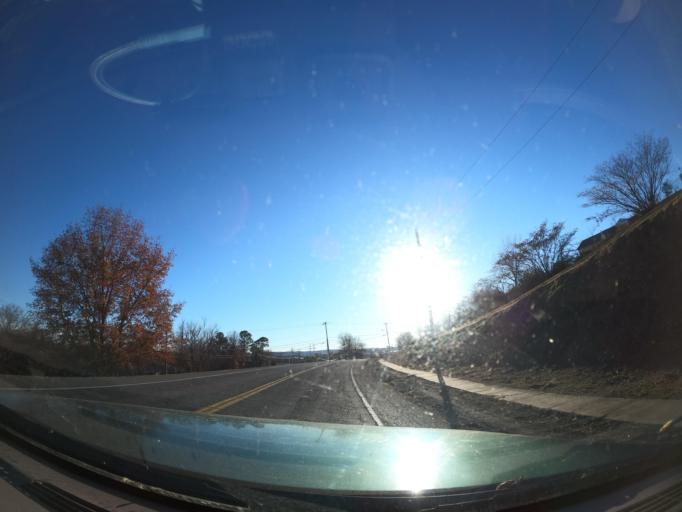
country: US
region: Oklahoma
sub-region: Latimer County
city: Wilburton
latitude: 34.9155
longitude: -95.3176
